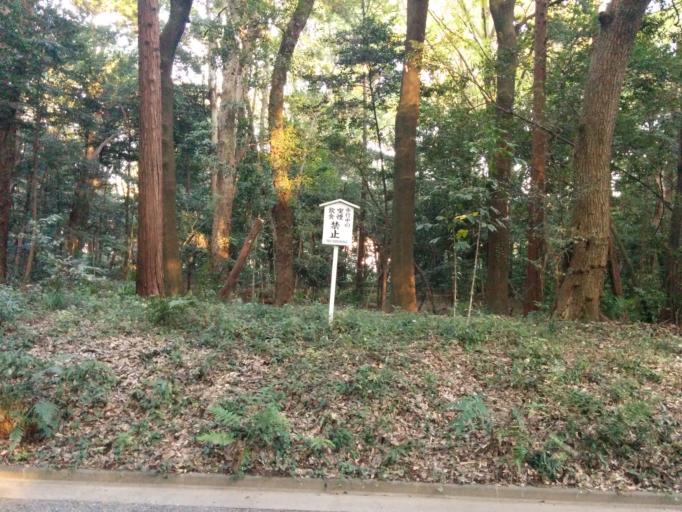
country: JP
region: Tokyo
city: Tokyo
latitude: 35.6774
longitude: 139.7021
